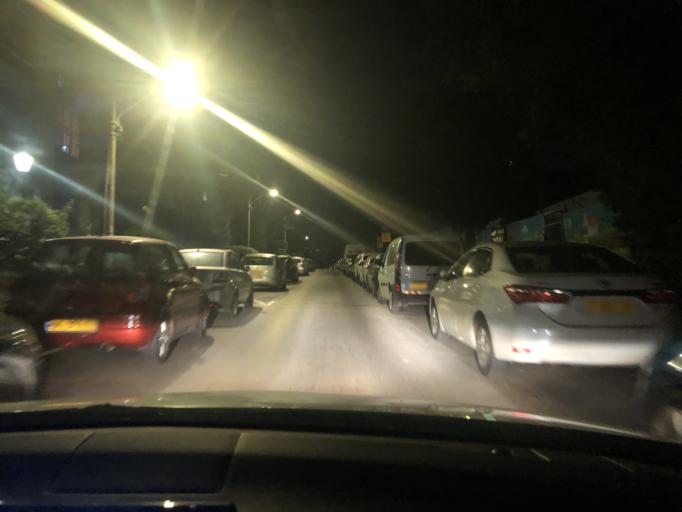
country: IL
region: Tel Aviv
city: Giv`atayim
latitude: 32.0603
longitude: 34.8251
